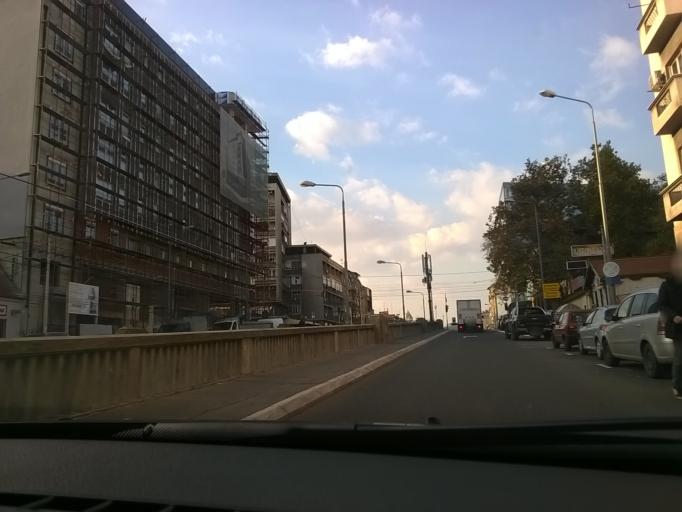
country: RS
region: Central Serbia
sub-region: Belgrade
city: Vracar
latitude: 44.8075
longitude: 20.4827
